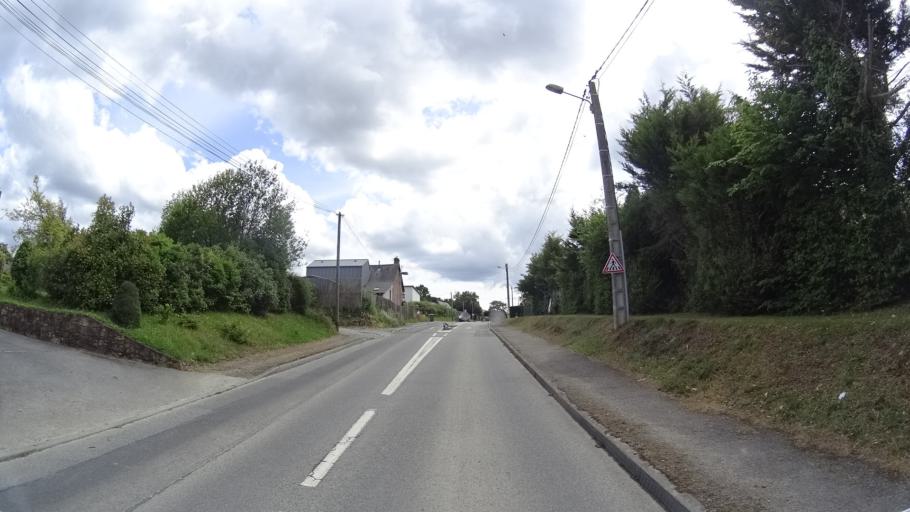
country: FR
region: Brittany
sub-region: Departement d'Ille-et-Vilaine
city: Laille
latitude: 47.9861
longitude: -1.7191
